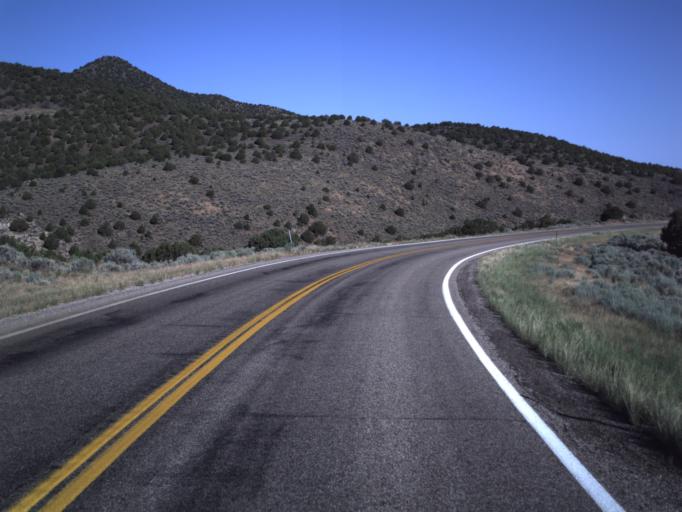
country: US
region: Utah
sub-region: Beaver County
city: Milford
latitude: 38.1123
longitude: -112.9501
